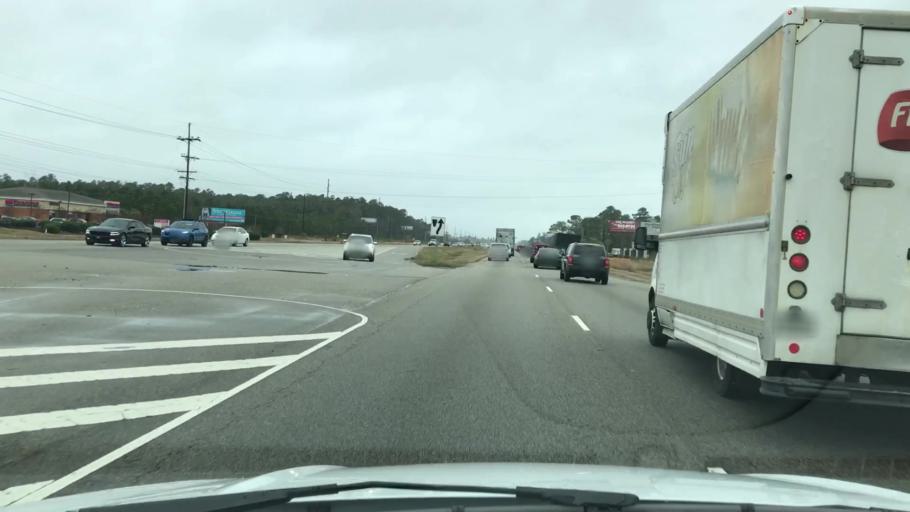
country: US
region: South Carolina
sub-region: Horry County
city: Red Hill
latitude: 33.7785
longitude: -78.9858
